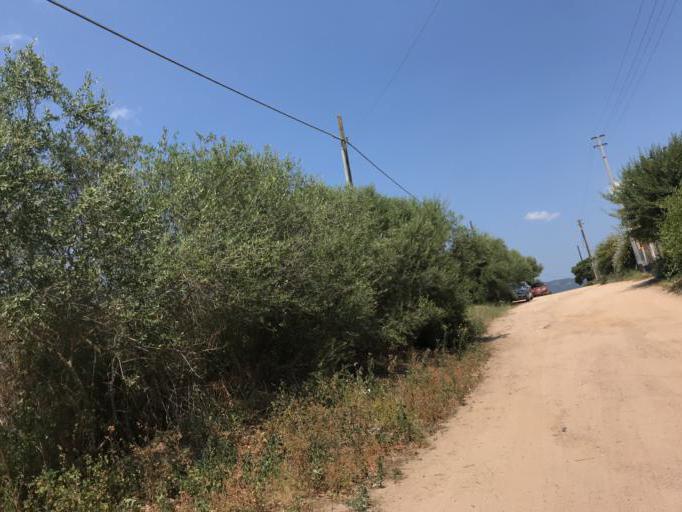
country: IT
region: Sardinia
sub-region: Provincia di Olbia-Tempio
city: Olbia
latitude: 40.9115
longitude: 9.5153
